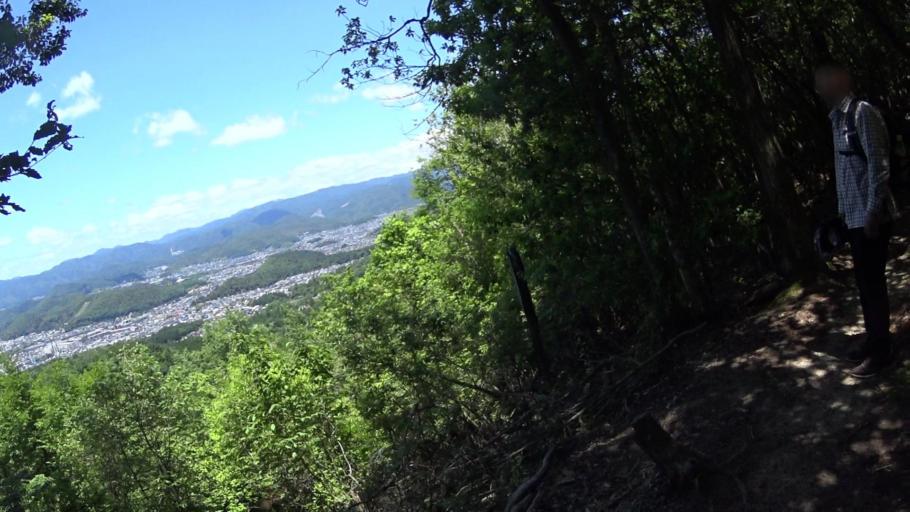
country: JP
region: Kyoto
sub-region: Kyoto-shi
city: Kamigyo-ku
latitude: 35.0439
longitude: 135.8090
